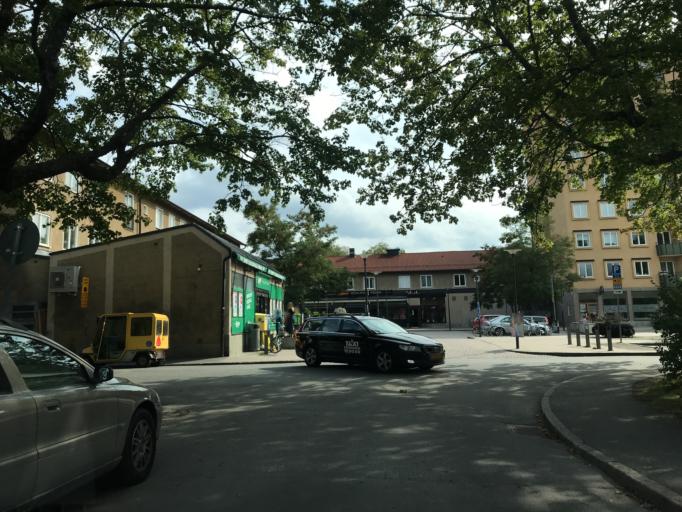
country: SE
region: Stockholm
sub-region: Stockholms Kommun
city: Arsta
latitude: 59.2876
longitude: 18.0096
